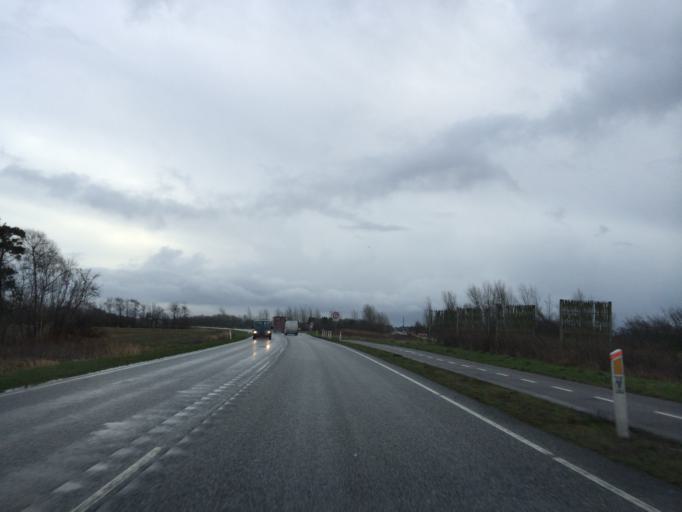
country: DK
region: Central Jutland
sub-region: Ringkobing-Skjern Kommune
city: Skjern
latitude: 55.9650
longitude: 8.4761
